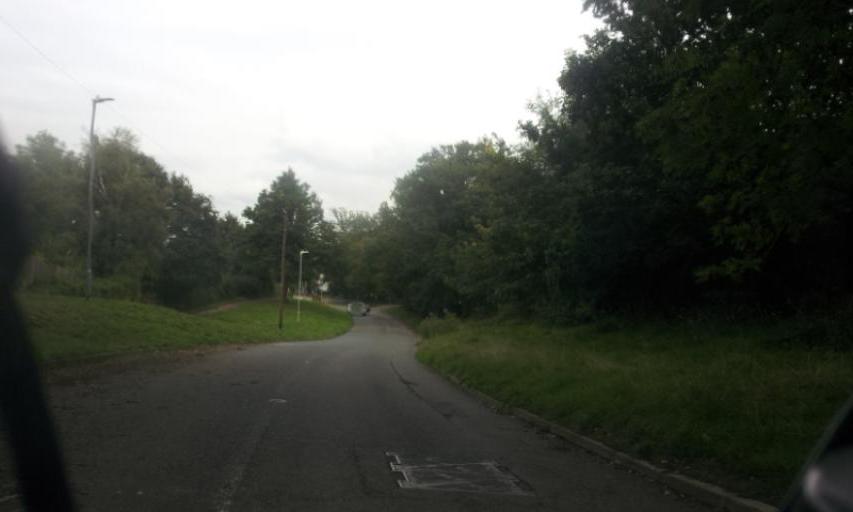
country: GB
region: England
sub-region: Kent
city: Tonbridge
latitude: 51.1849
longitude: 0.2854
